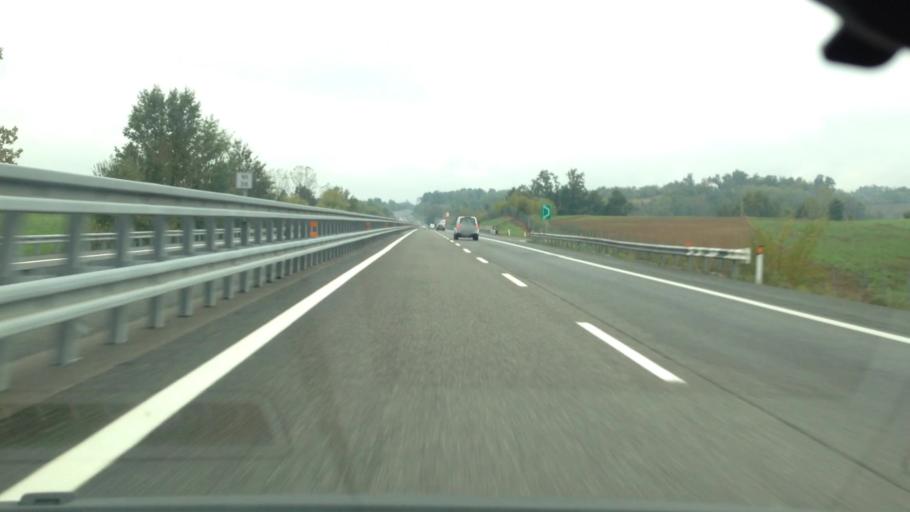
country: IT
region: Piedmont
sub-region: Provincia di Asti
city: Revigliasco d'Asti
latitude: 44.9037
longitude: 8.1527
